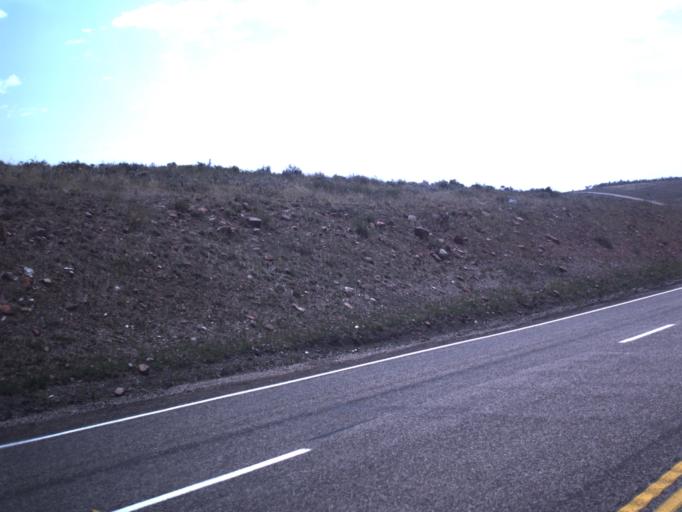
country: US
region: Utah
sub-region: Uintah County
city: Maeser
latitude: 40.6895
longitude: -109.4950
